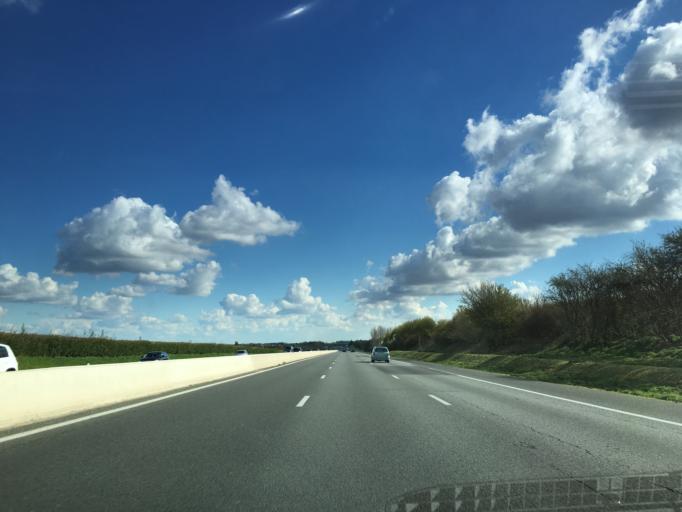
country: FR
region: Nord-Pas-de-Calais
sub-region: Departement du Pas-de-Calais
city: Croisilles
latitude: 50.2119
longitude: 2.8630
